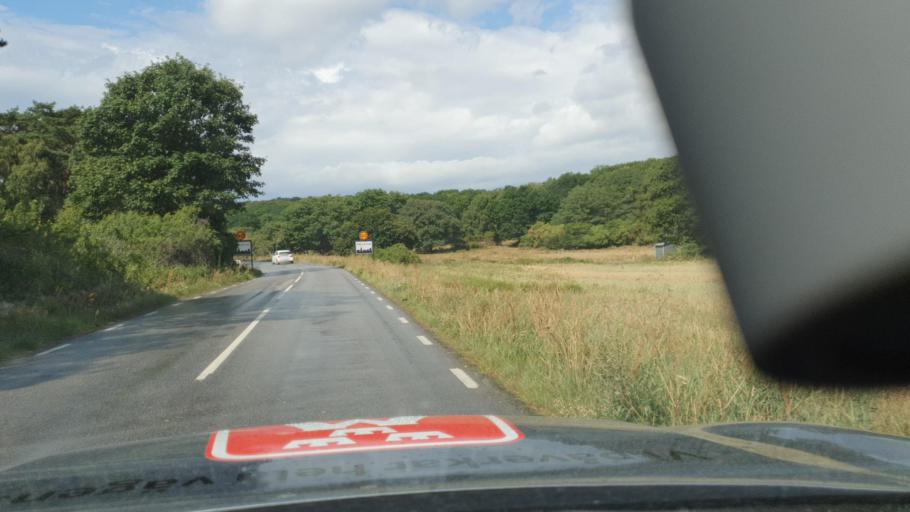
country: SE
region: Blekinge
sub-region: Solvesborgs Kommun
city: Soelvesborg
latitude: 56.0171
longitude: 14.7048
